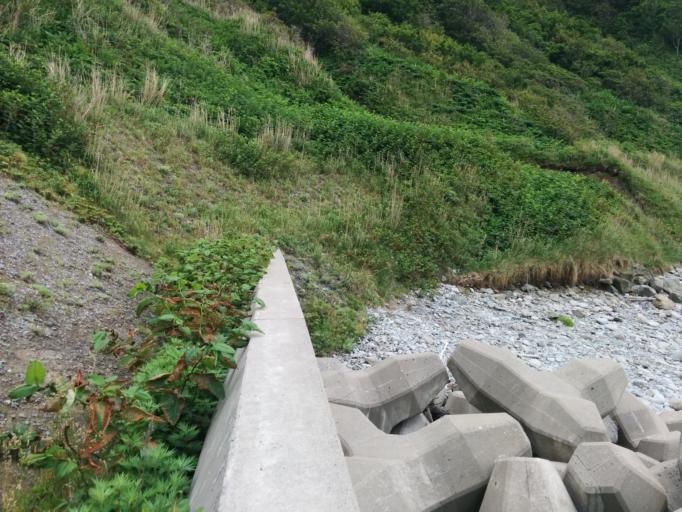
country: JP
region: Hokkaido
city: Iwanai
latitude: 42.3118
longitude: 139.7696
